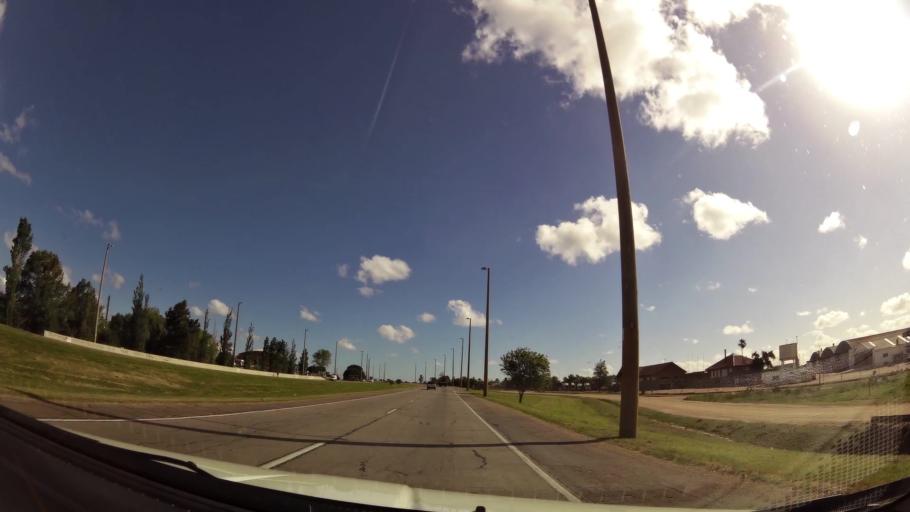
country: UY
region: Canelones
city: La Paz
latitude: -34.8306
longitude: -56.2526
